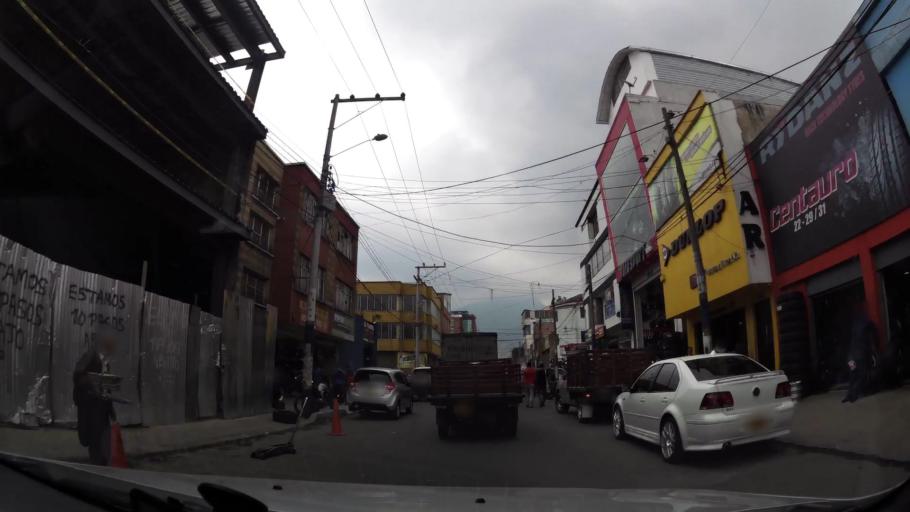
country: CO
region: Bogota D.C.
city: Bogota
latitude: 4.6046
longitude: -74.0910
